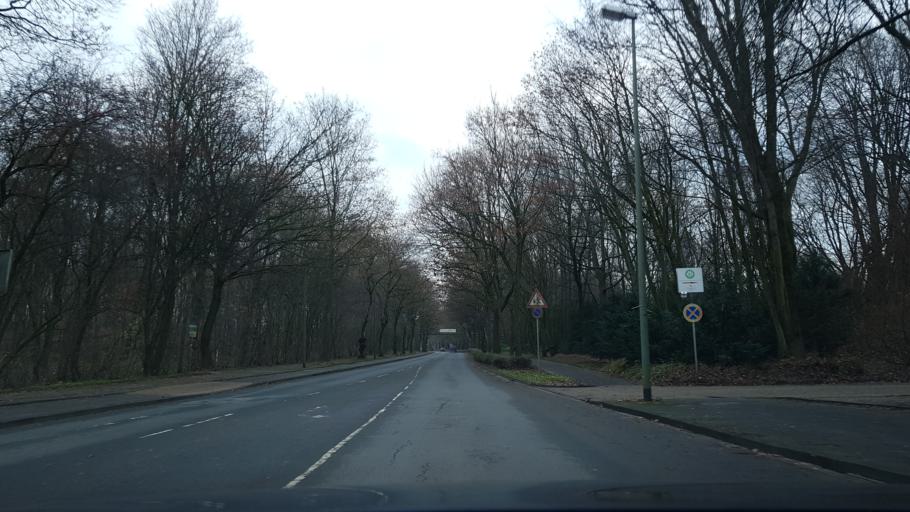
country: DE
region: North Rhine-Westphalia
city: Meiderich
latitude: 51.5179
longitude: 6.7768
